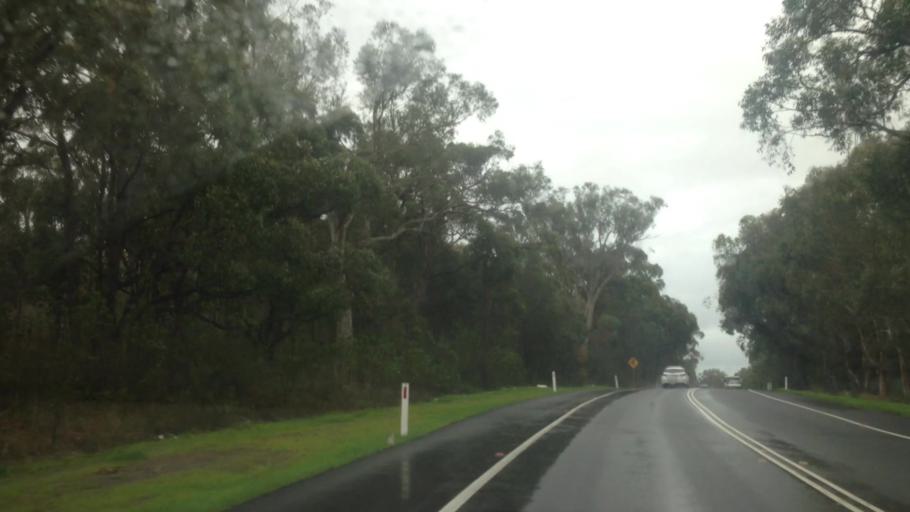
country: AU
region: New South Wales
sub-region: Lake Macquarie Shire
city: Dora Creek
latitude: -33.1237
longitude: 151.4755
